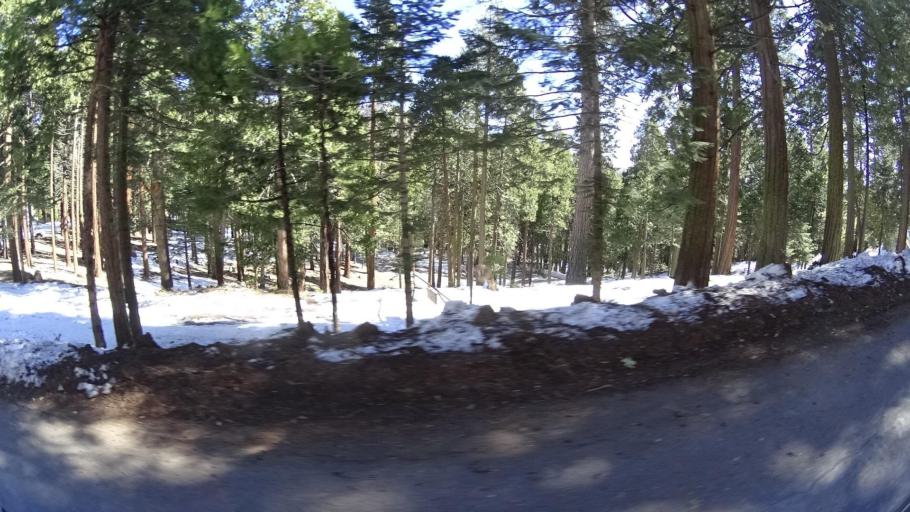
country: US
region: California
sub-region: Kern County
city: Alta Sierra
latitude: 35.7371
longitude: -118.5573
